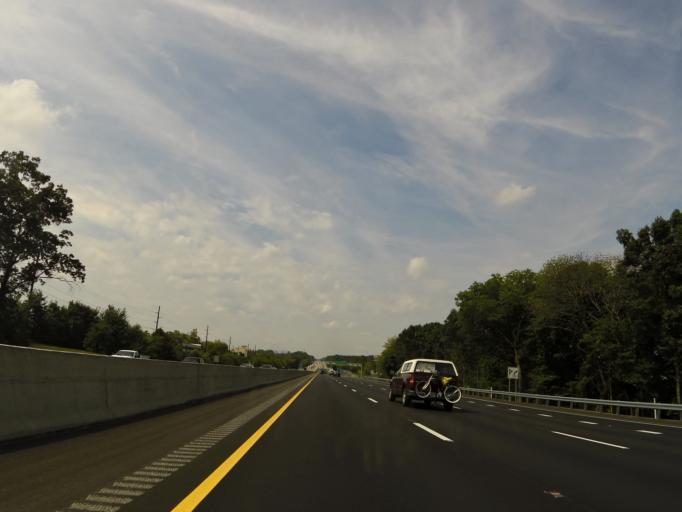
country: US
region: Tennessee
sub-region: Knox County
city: Farragut
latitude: 35.9010
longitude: -84.1660
